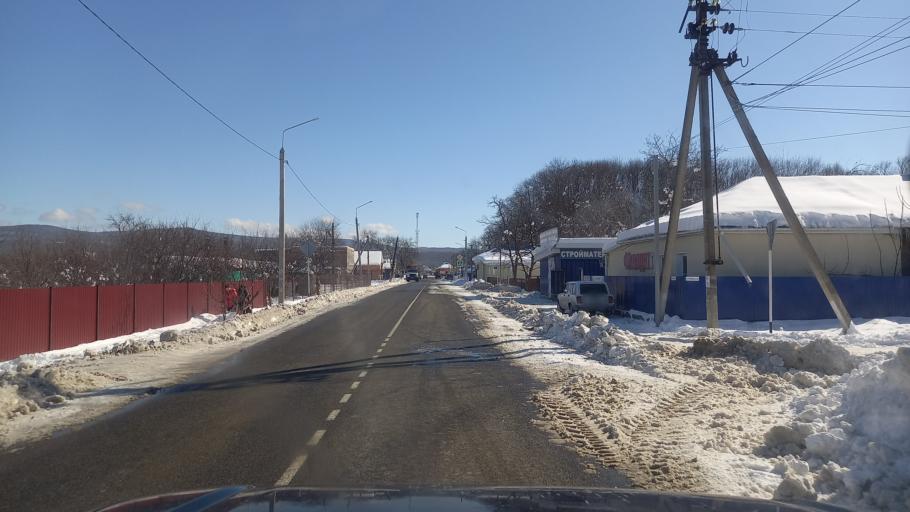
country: RU
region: Adygeya
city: Abadzekhskaya
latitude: 44.3919
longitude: 40.2177
